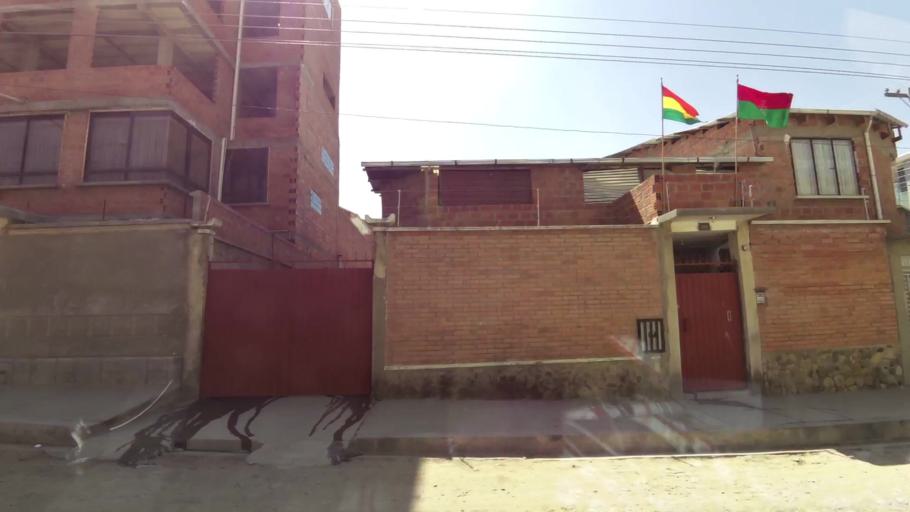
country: BO
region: La Paz
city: La Paz
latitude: -16.5403
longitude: -68.0499
